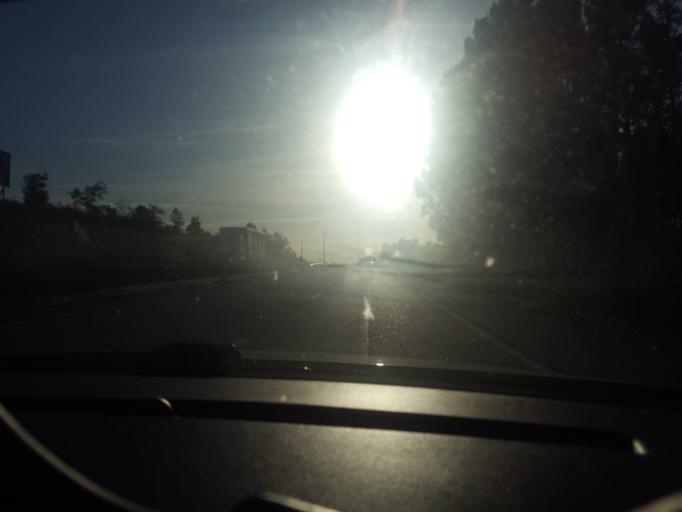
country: PT
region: Viseu
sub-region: Concelho de Carregal do Sal
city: Carregal do Sal
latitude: 40.4622
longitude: -7.9554
